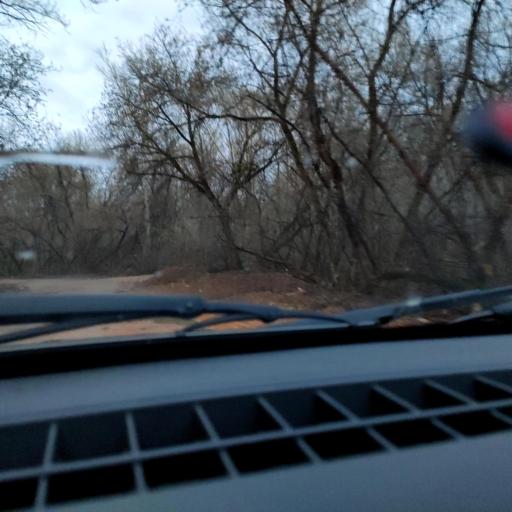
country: RU
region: Bashkortostan
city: Ufa
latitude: 54.6762
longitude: 55.9737
